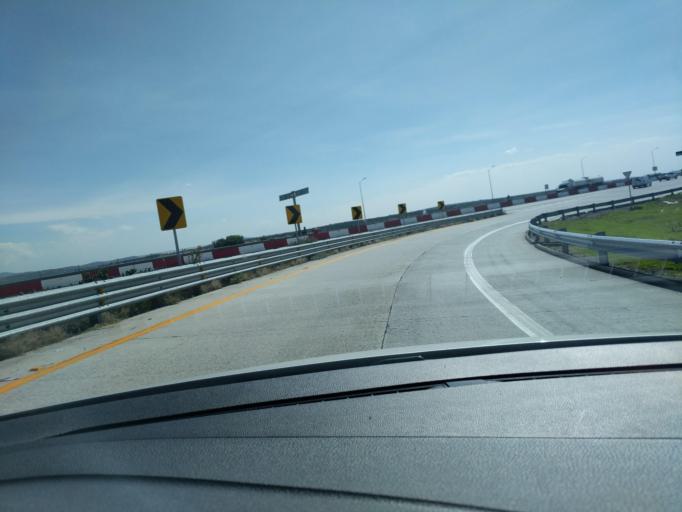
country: MX
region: Hidalgo
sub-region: Tolcayuca
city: Vicente Guerrero (San Javier)
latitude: 19.9283
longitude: -98.8898
